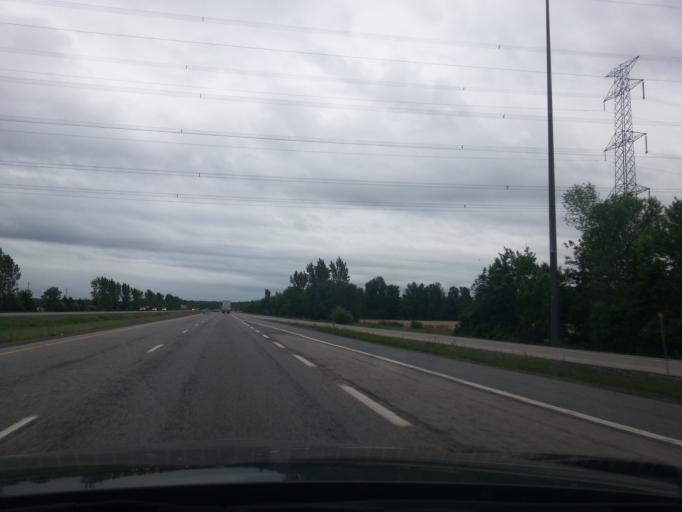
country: CA
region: Ontario
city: Bells Corners
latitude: 45.3102
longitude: -75.7996
